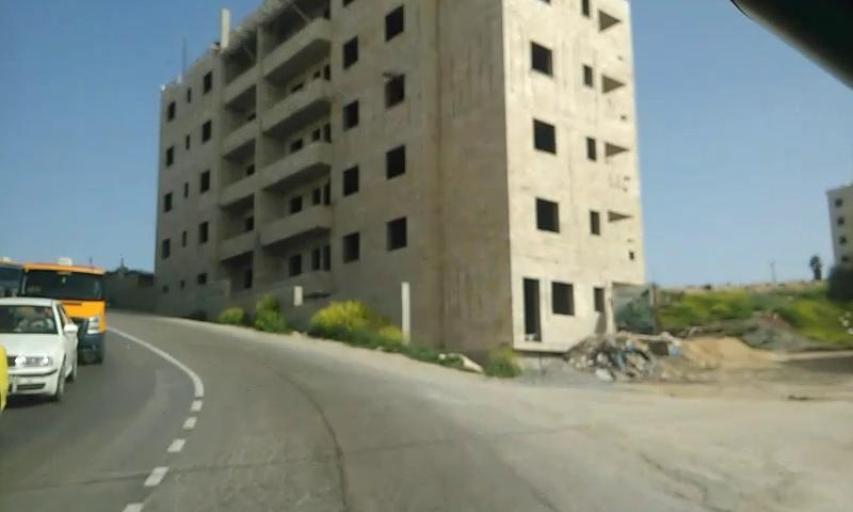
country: PS
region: West Bank
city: Surda
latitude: 31.9351
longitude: 35.2073
